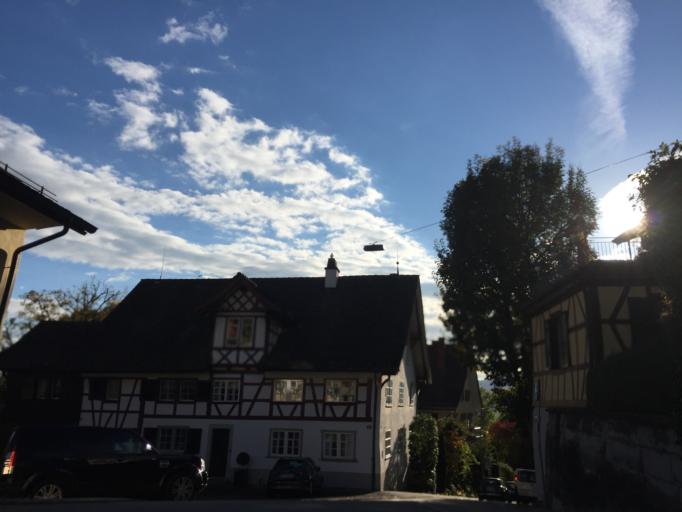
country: CH
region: Zurich
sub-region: Bezirk Zuerich
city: Zuerich (Kreis 7) / Fluntern
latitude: 47.3754
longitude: 8.5594
